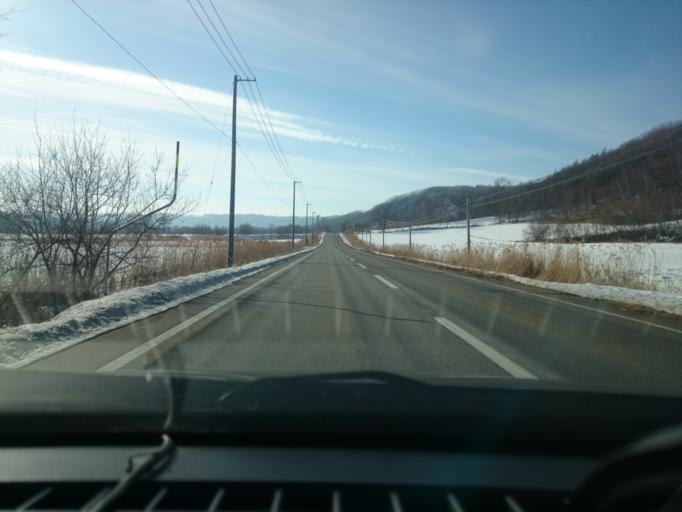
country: JP
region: Hokkaido
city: Otofuke
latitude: 43.2611
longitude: 143.5757
